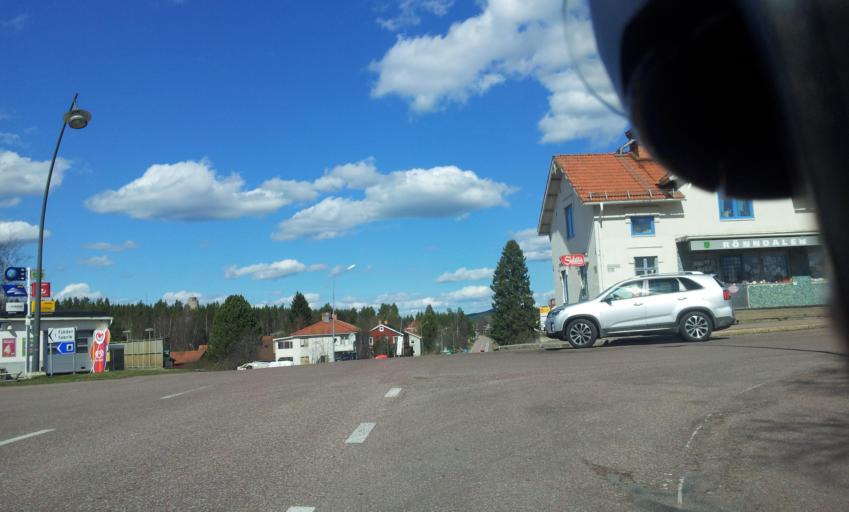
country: SE
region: Dalarna
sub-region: Faluns Kommun
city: Svardsjo
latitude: 60.8078
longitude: 15.7578
